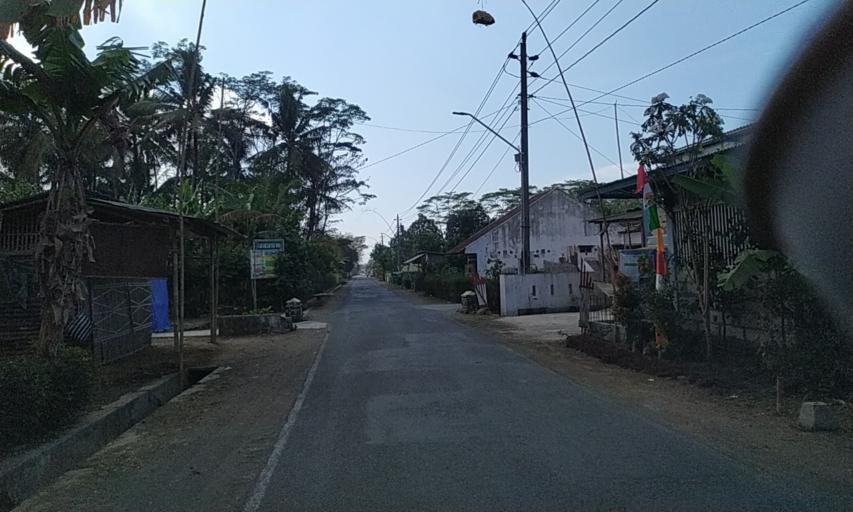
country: ID
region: Central Java
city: Adipala
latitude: -7.6639
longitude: 109.1617
